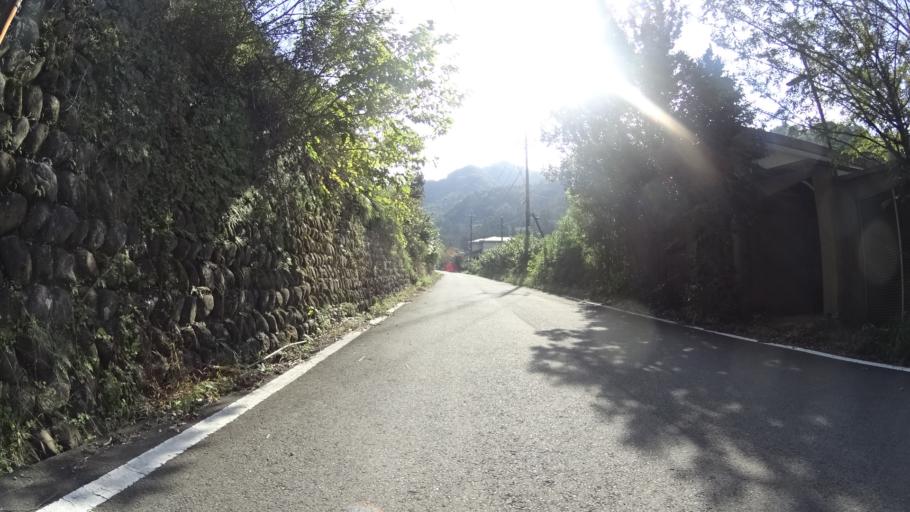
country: JP
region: Yamanashi
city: Otsuki
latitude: 35.5847
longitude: 138.9690
